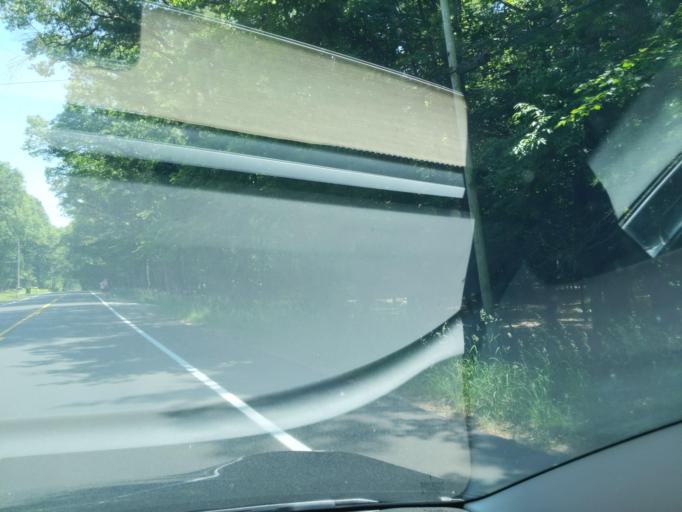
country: US
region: Michigan
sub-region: Muskegon County
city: Montague
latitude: 43.3833
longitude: -86.4209
